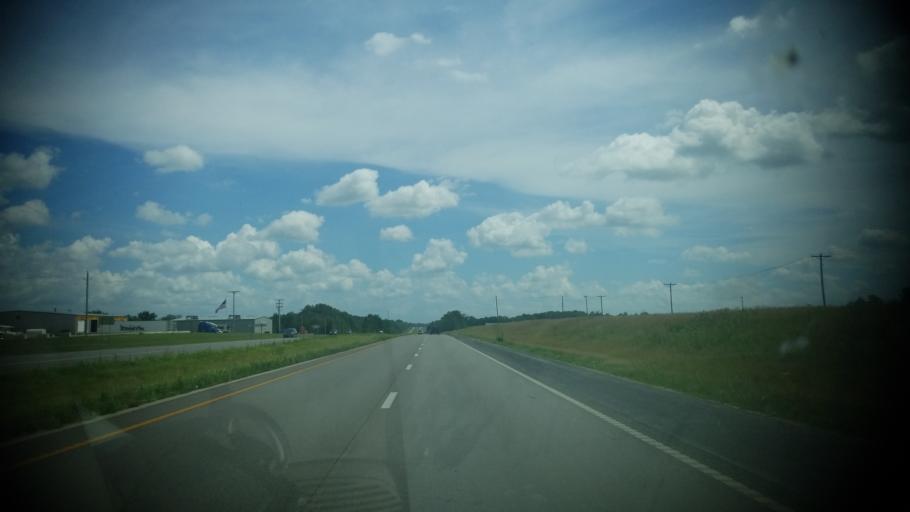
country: US
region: Missouri
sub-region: Lincoln County
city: Troy
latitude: 39.0690
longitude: -90.9738
